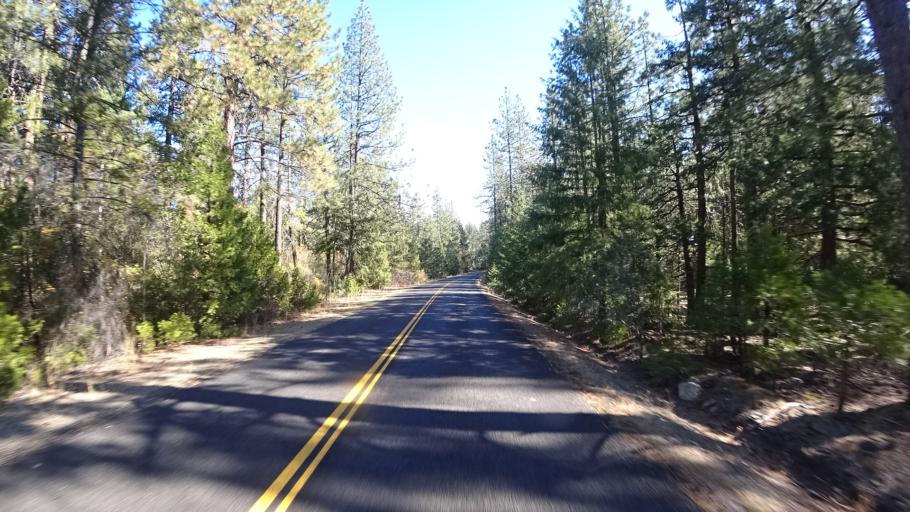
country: US
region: California
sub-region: Siskiyou County
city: Weed
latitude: 41.4343
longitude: -122.4724
